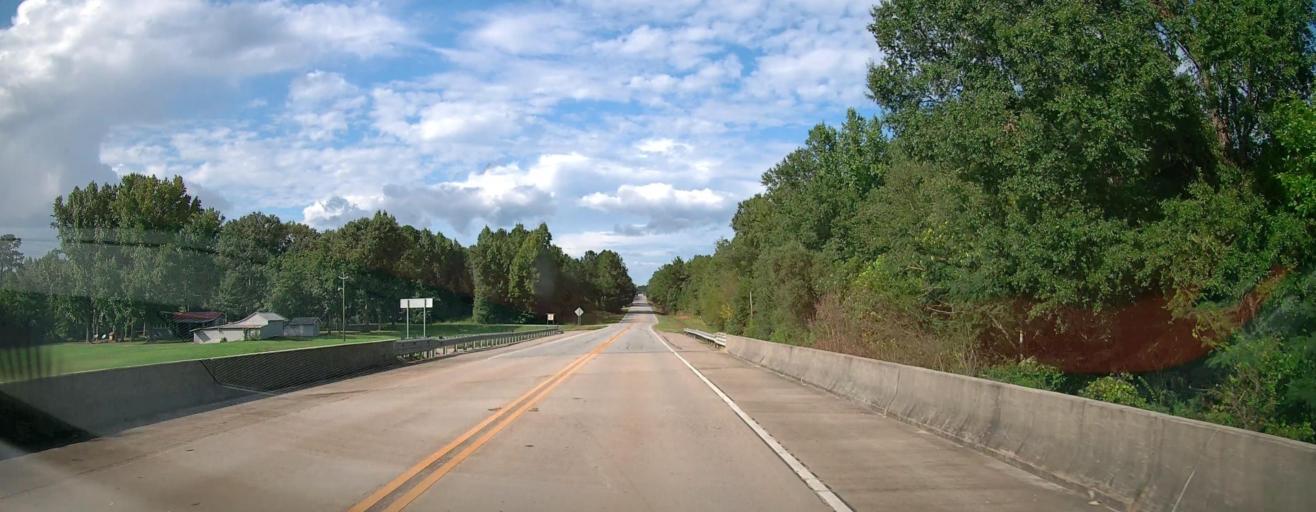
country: US
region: Georgia
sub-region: Meriwether County
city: Greenville
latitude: 32.9986
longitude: -84.5713
